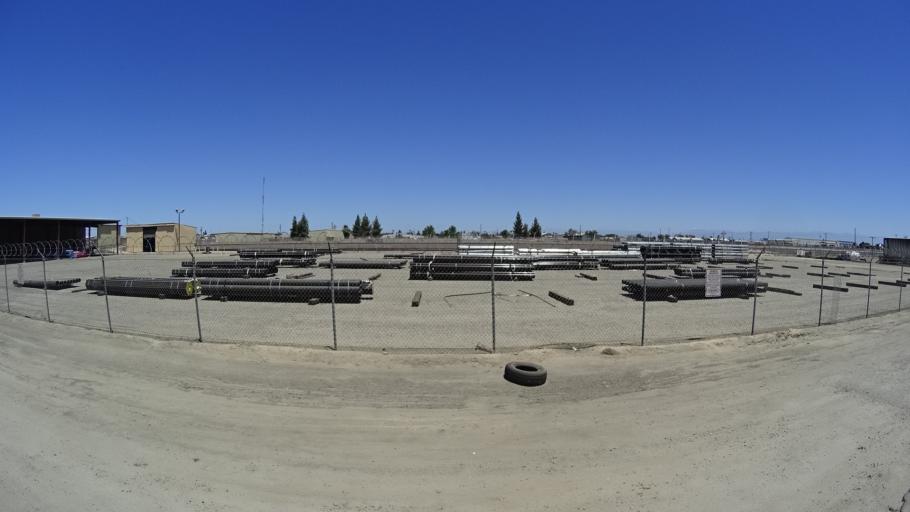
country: US
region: California
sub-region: Fresno County
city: Fresno
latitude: 36.6987
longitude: -119.7399
